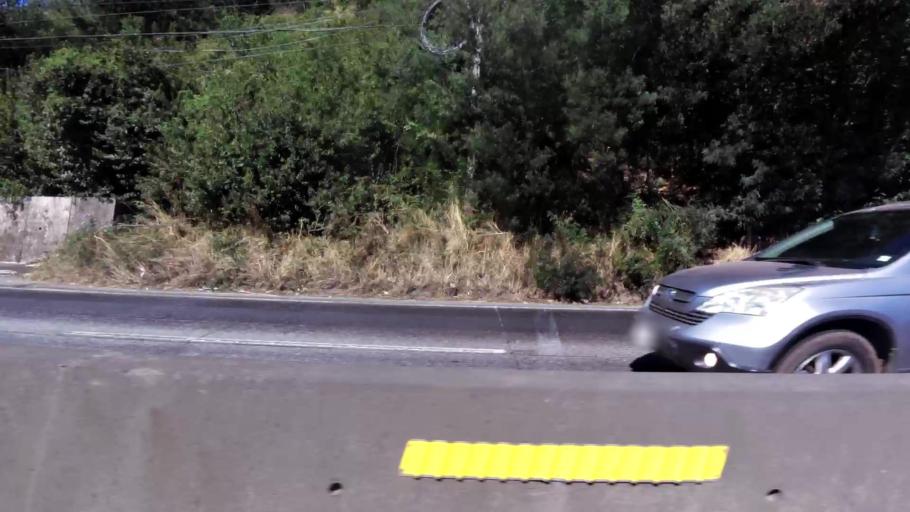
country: CL
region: Biobio
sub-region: Provincia de Concepcion
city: Concepcion
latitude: -36.8023
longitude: -73.0256
